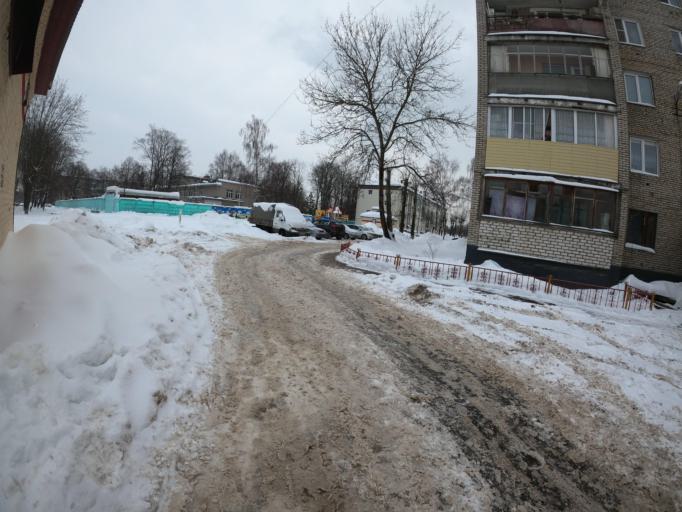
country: RU
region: Moskovskaya
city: Elektrogorsk
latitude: 55.8680
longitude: 38.7813
